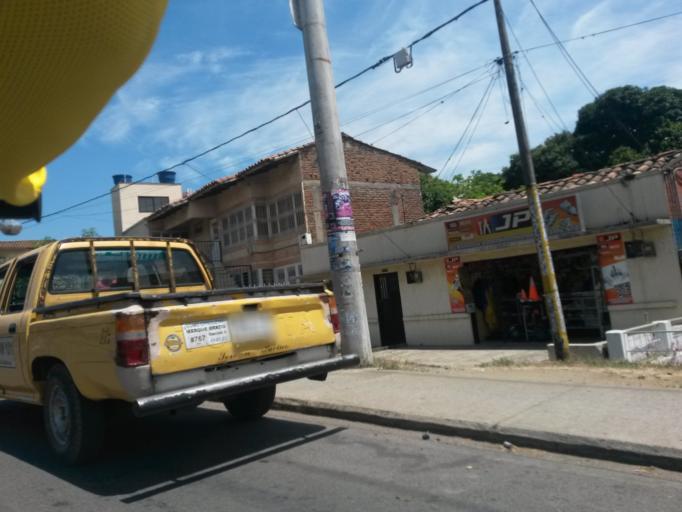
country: CO
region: Cauca
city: Santander de Quilichao
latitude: 3.0112
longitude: -76.4844
